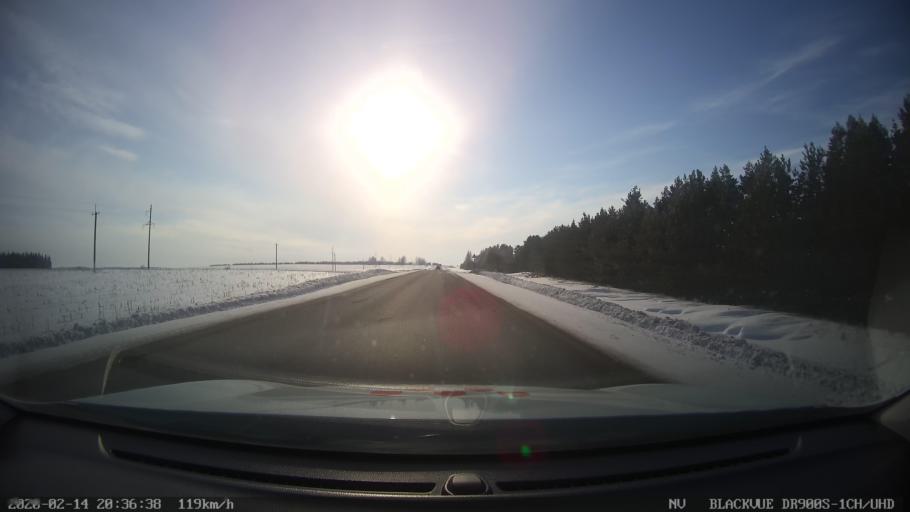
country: RU
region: Tatarstan
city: Kuybyshevskiy Zaton
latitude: 55.3640
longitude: 49.0013
